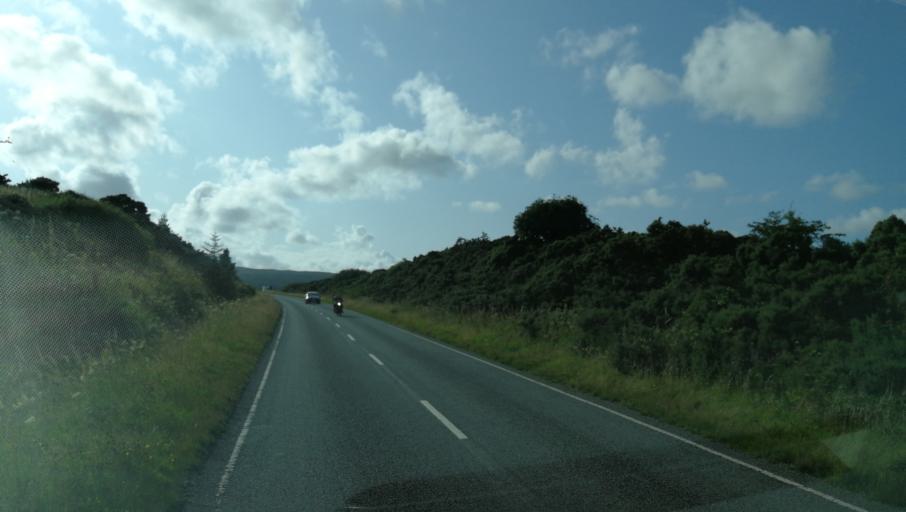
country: GB
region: Scotland
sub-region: Highland
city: Isle of Skye
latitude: 57.4720
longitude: -6.4427
